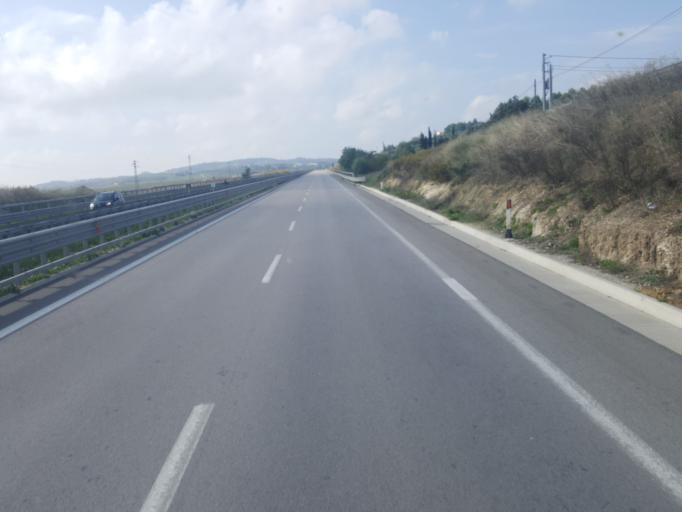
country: IT
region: Sicily
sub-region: Provincia di Caltanissetta
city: Serradifalco
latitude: 37.4140
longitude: 13.8970
